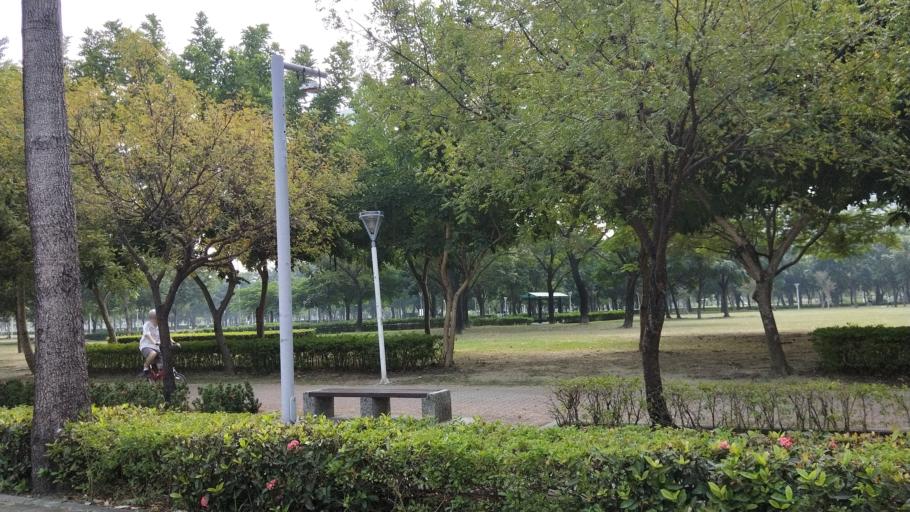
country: TW
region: Kaohsiung
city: Kaohsiung
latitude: 22.6611
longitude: 120.2978
